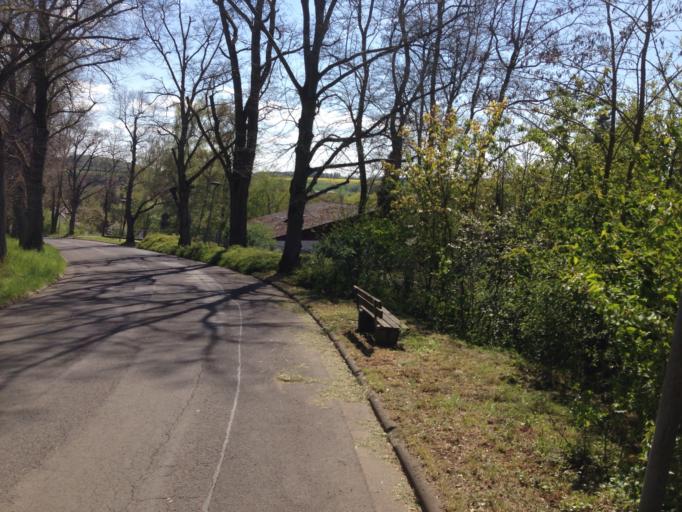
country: DE
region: Hesse
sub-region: Regierungsbezirk Giessen
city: Laubach
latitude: 50.5483
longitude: 8.9905
